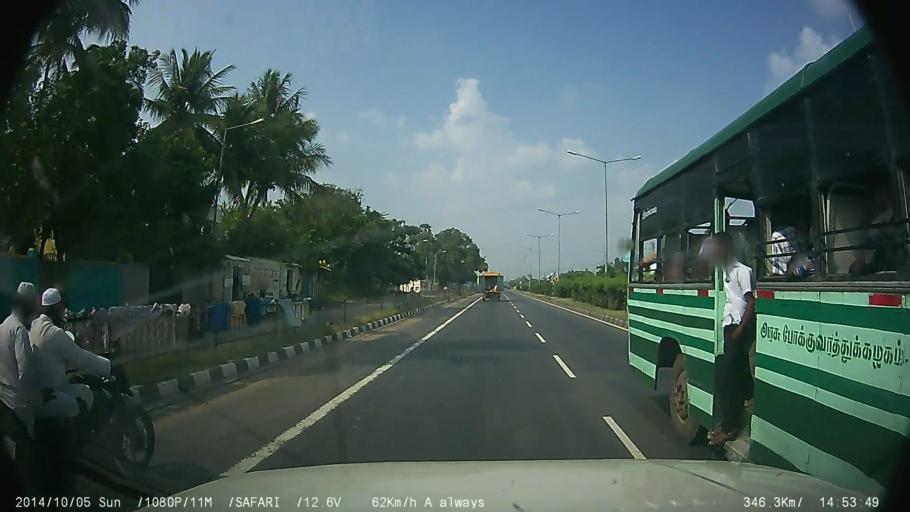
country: IN
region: Tamil Nadu
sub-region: Kancheepuram
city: Madurantakam
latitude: 12.5405
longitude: 79.9043
